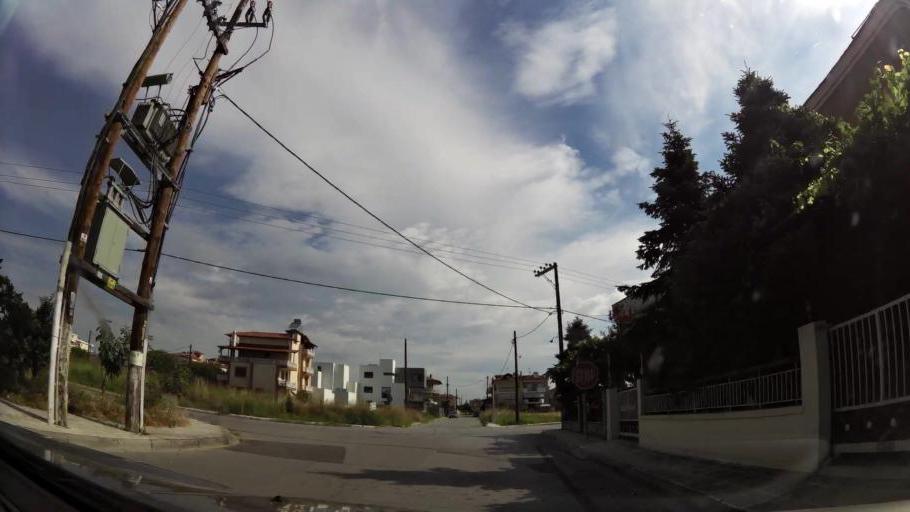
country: GR
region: Central Macedonia
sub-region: Nomos Pierias
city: Katerini
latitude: 40.2831
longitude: 22.5083
